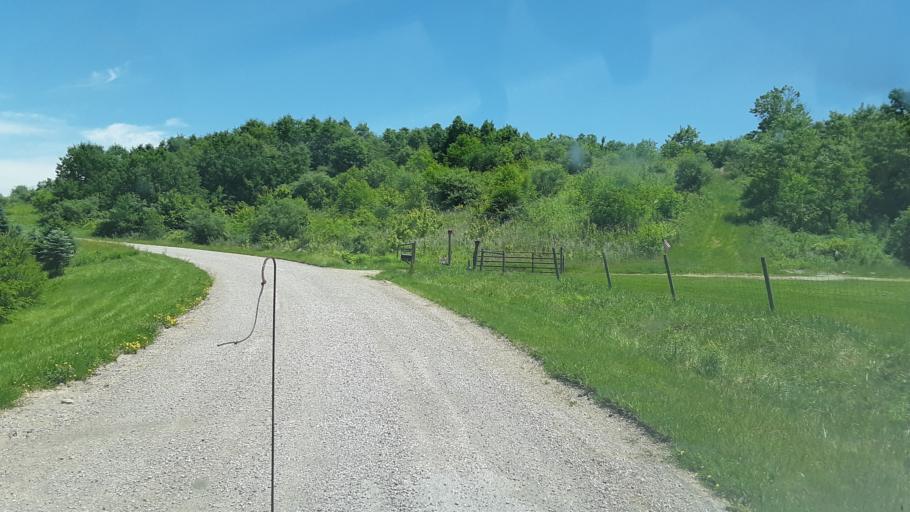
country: US
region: Ohio
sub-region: Coshocton County
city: Coshocton
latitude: 40.2740
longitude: -81.9776
